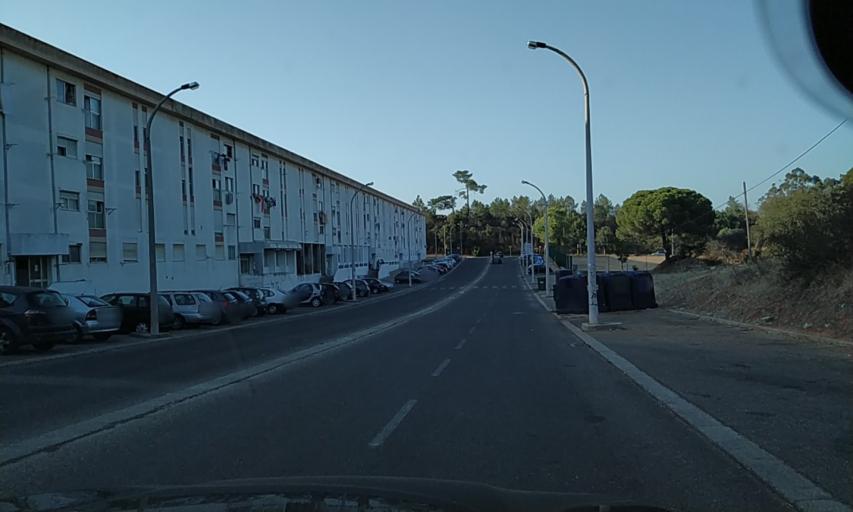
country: PT
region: Setubal
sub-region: Setubal
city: Setubal
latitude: 38.5210
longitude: -8.8598
